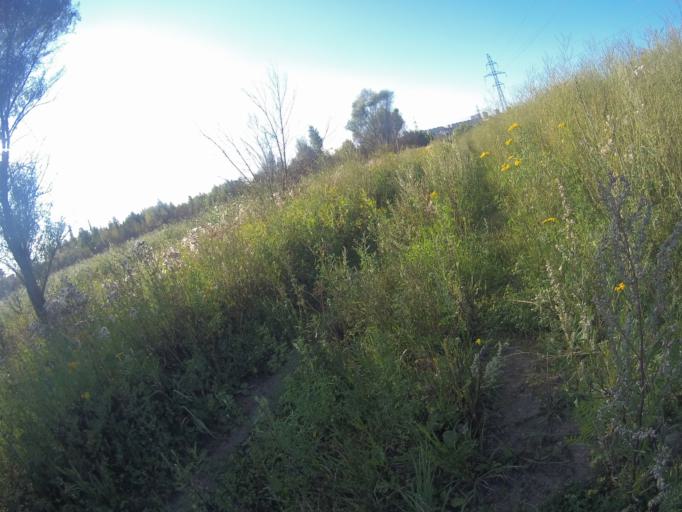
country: RU
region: Vladimir
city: Kommunar
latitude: 56.1433
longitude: 40.4784
